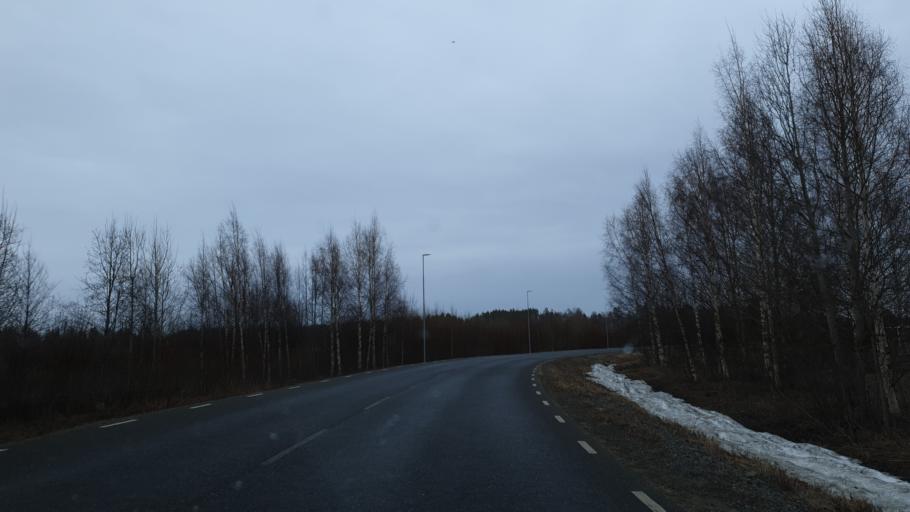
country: SE
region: Vaesterbotten
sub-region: Skelleftea Kommun
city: Kage
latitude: 64.8376
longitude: 20.9917
